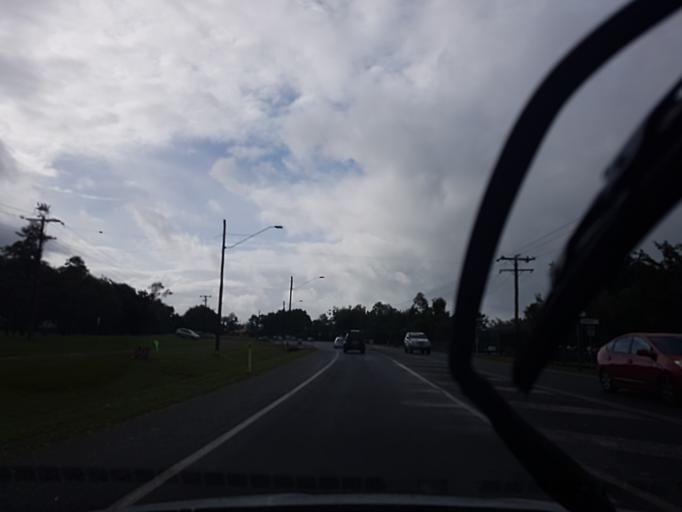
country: AU
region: Queensland
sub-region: Cairns
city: Trinity Beach
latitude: -16.7760
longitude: 145.6752
